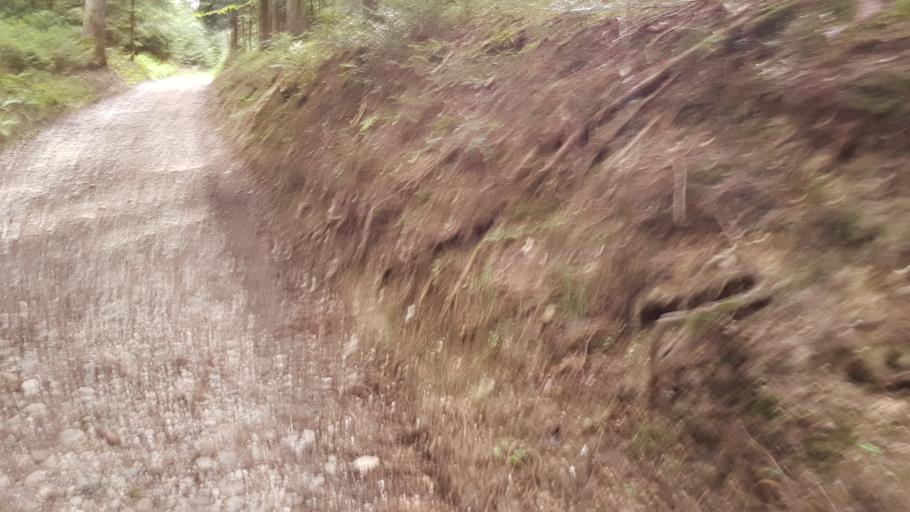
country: CH
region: Lucerne
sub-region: Entlebuch District
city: Oberdiessbach
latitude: 46.8560
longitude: 7.6397
